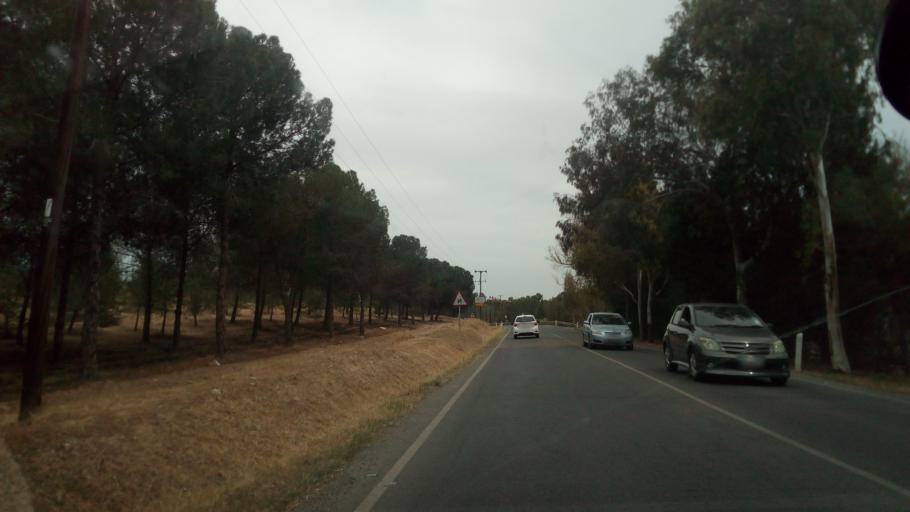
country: CY
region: Lefkosia
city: Nicosia
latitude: 35.1377
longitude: 33.3790
